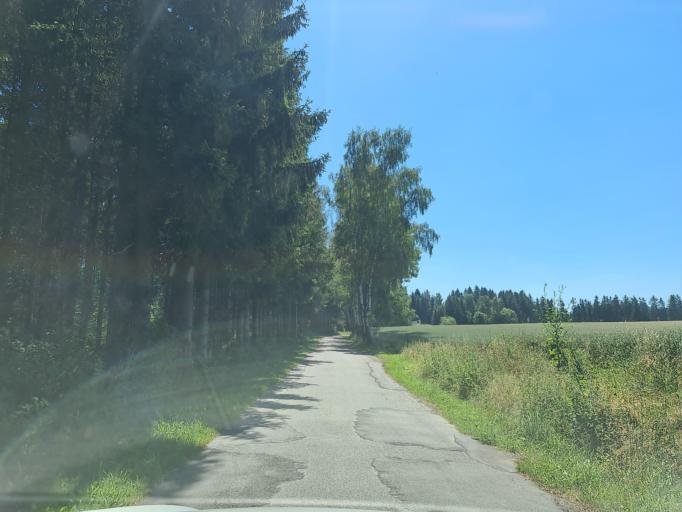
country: DE
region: Saxony
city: Neuhausen
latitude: 50.6974
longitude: 13.5002
